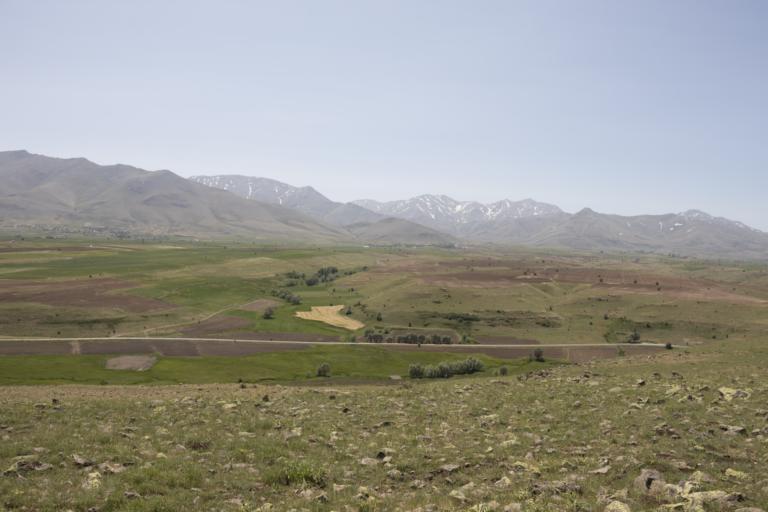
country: TR
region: Kayseri
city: Toklar
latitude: 38.4528
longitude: 36.0614
